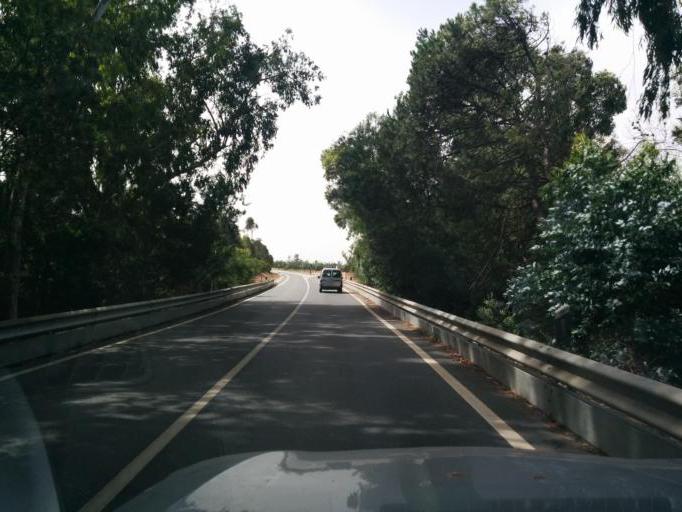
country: PT
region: Beja
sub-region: Odemira
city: Vila Nova de Milfontes
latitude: 37.6448
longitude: -8.7596
